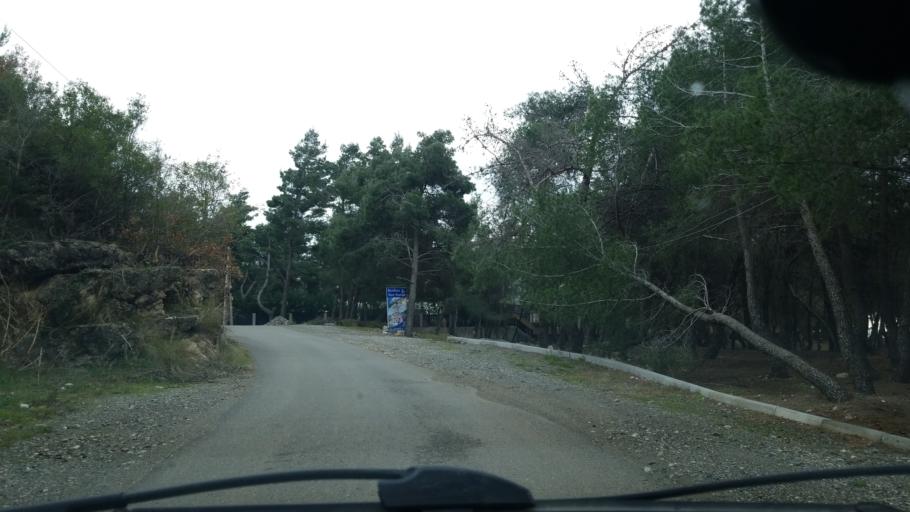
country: AL
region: Lezhe
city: Shengjin
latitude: 41.8219
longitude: 19.5617
